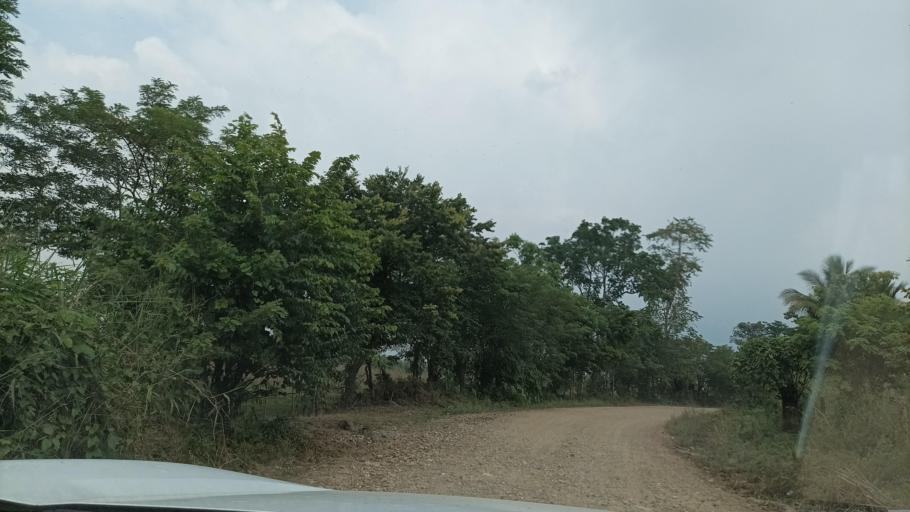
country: MX
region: Veracruz
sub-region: Moloacan
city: Cuichapa
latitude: 17.5809
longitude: -94.2220
